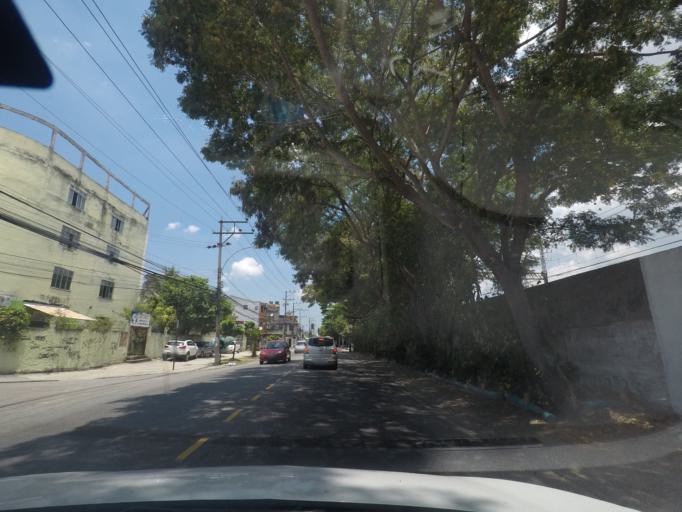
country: BR
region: Rio de Janeiro
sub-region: Sao Joao De Meriti
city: Sao Joao de Meriti
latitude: -22.8669
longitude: -43.3537
